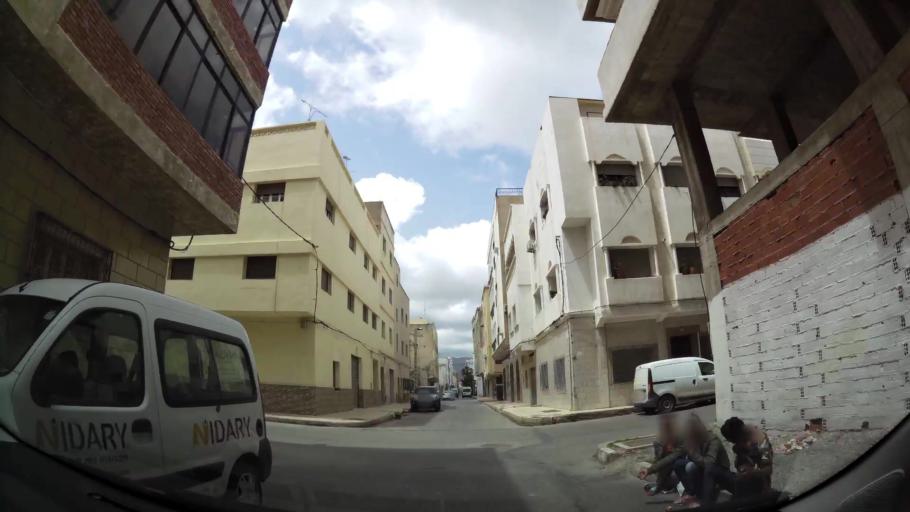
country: MA
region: Oriental
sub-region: Nador
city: Nador
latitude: 35.1792
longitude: -2.9221
